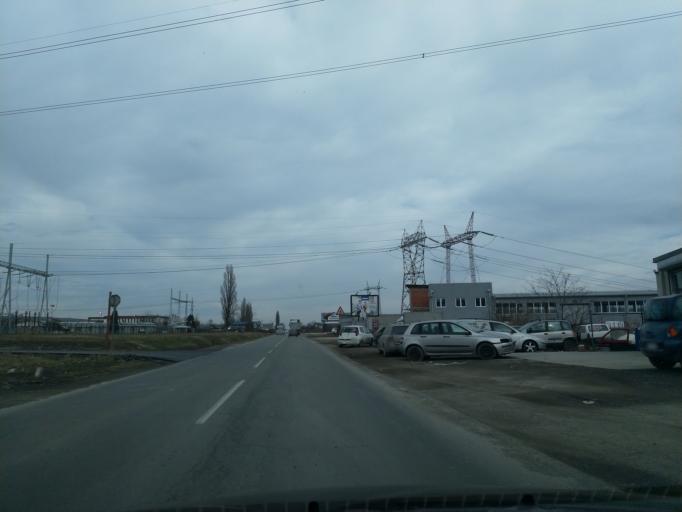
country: RS
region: Central Serbia
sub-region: Belgrade
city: Zvezdara
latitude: 44.7339
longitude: 20.5882
